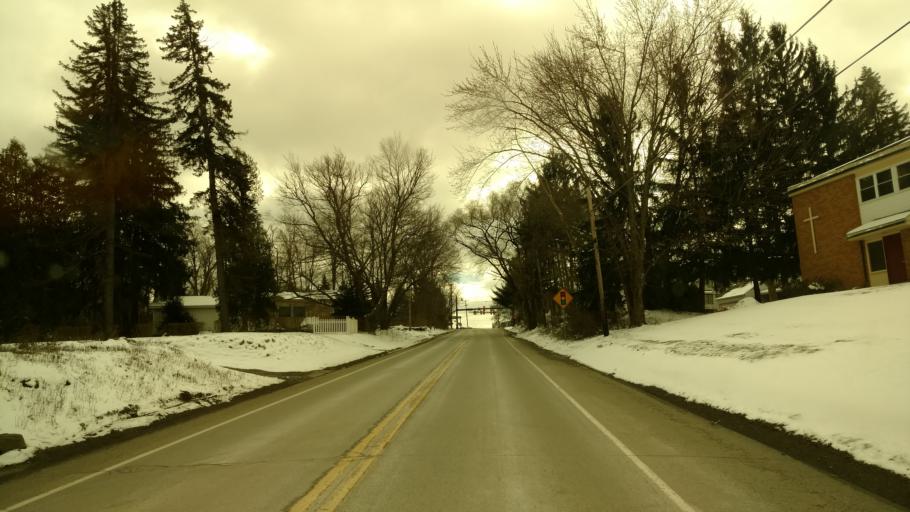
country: US
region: Pennsylvania
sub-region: Mercer County
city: Mercer
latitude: 41.2319
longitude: -80.2392
